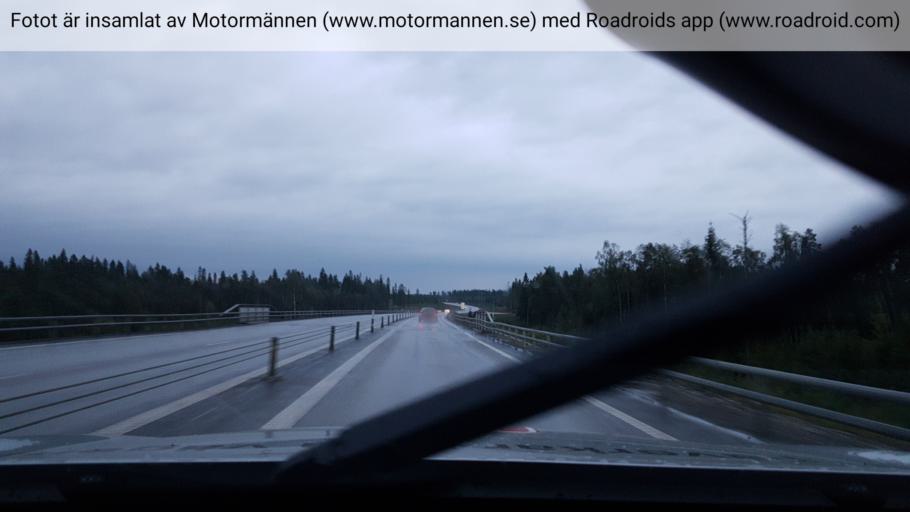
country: SE
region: Vaesterbotten
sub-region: Umea Kommun
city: Umea
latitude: 63.8580
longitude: 20.2518
